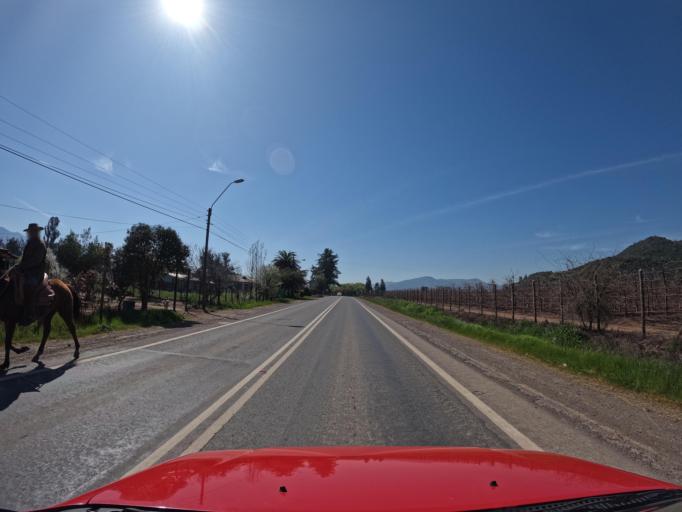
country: CL
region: Maule
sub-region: Provincia de Curico
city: Rauco
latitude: -35.0494
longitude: -71.4694
